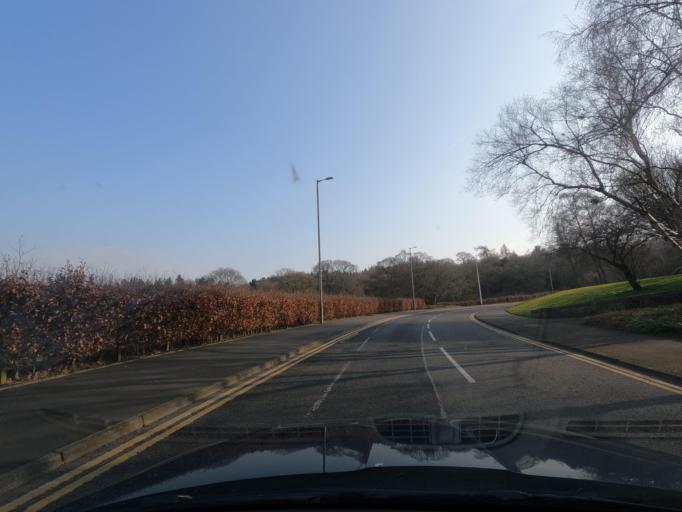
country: GB
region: Scotland
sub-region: Falkirk
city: Falkirk
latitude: 55.9946
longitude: -3.7781
